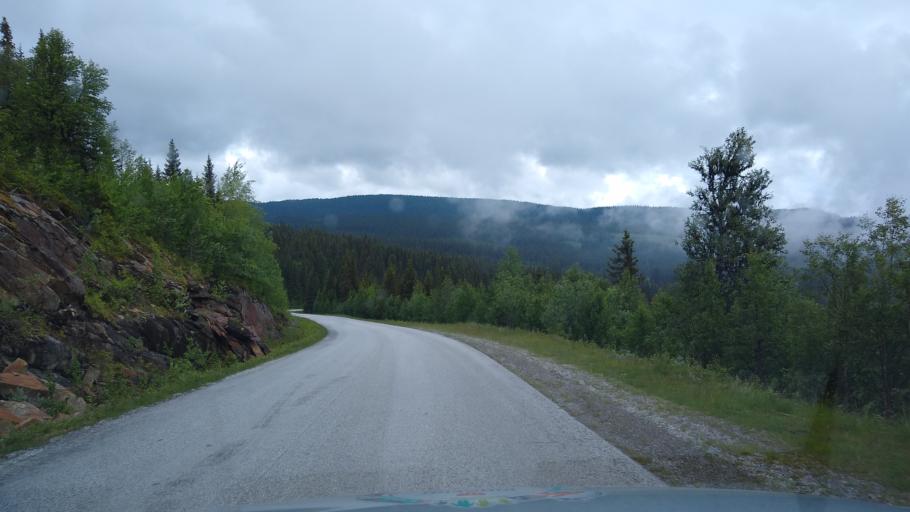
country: NO
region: Oppland
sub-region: Ringebu
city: Ringebu
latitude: 61.4835
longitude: 10.1203
